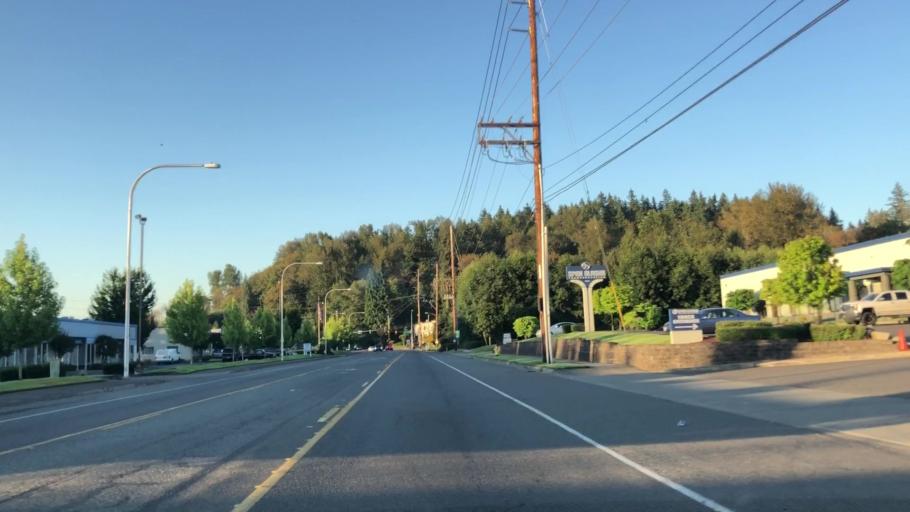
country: US
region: Washington
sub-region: King County
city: Lakeland North
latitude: 47.3427
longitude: -122.2499
